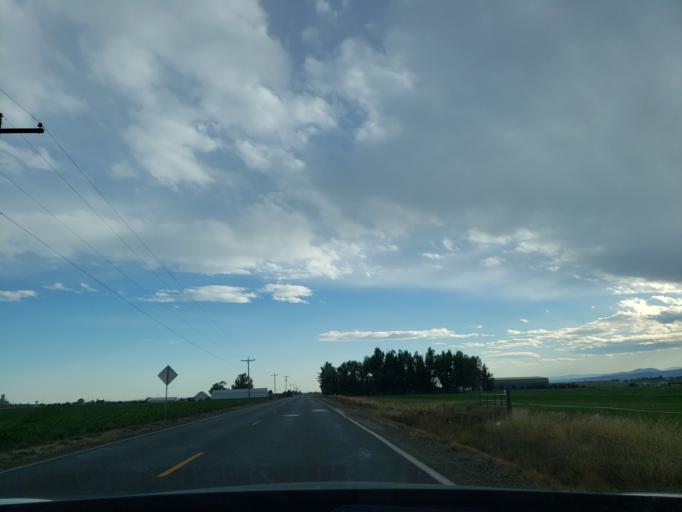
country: US
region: Colorado
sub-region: Larimer County
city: Wellington
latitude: 40.6372
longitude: -105.0197
